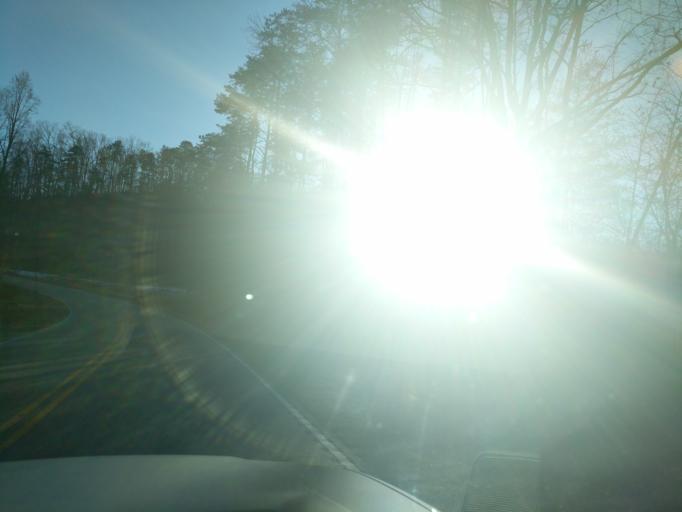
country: US
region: South Carolina
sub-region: Oconee County
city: Westminster
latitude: 34.7415
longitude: -83.2389
